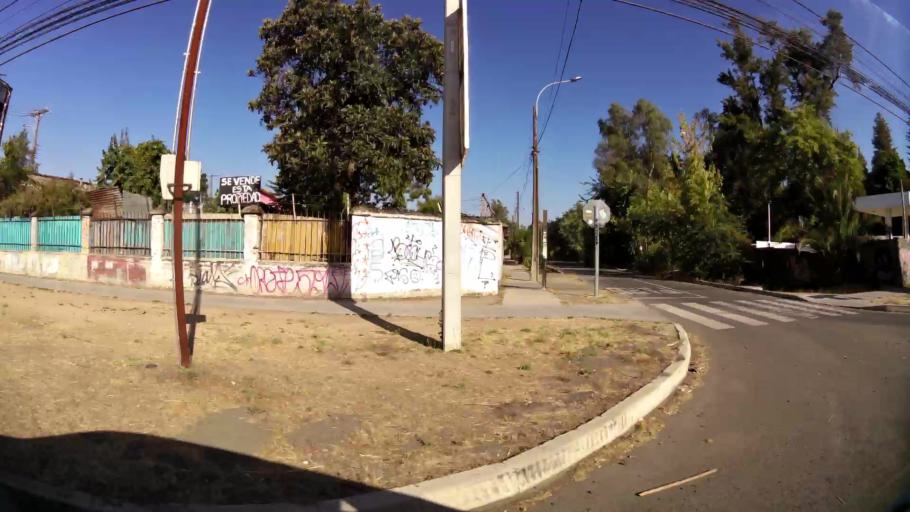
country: CL
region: Maule
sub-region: Provincia de Talca
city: Talca
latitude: -35.4321
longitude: -71.6777
